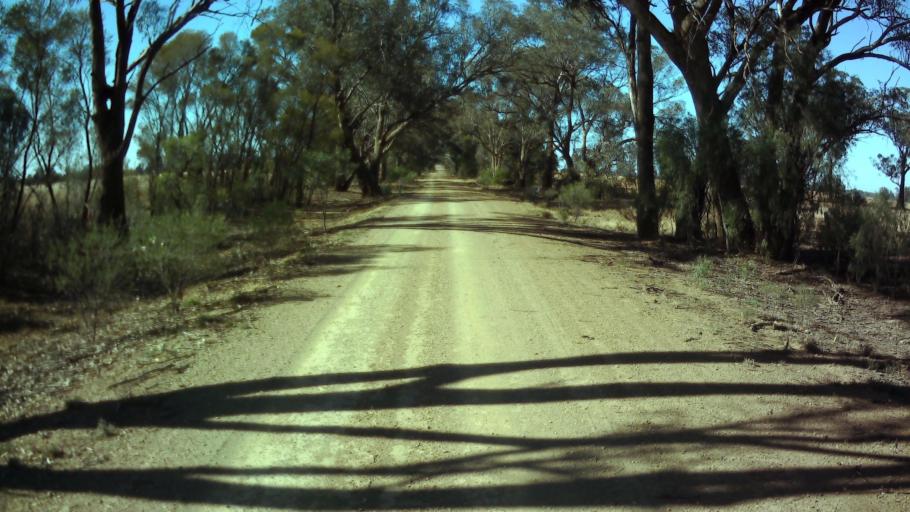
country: AU
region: New South Wales
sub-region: Weddin
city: Grenfell
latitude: -33.9202
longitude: 147.8749
